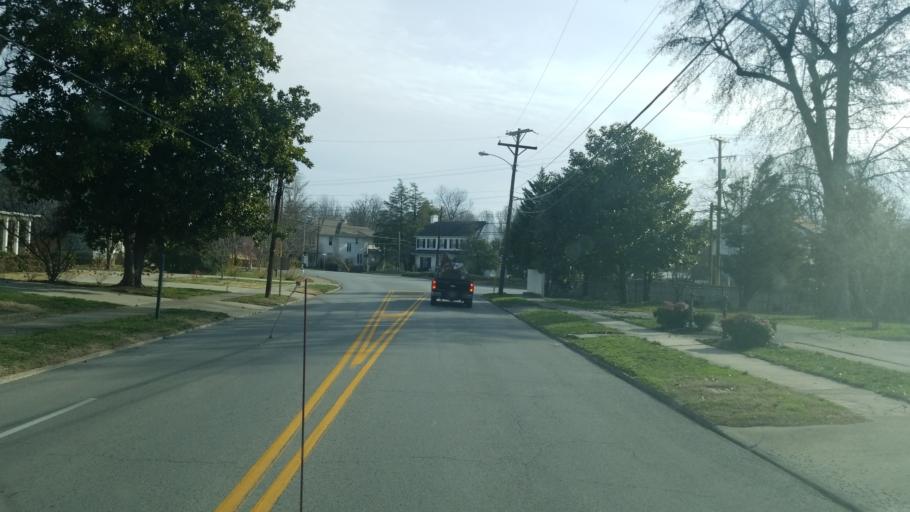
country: US
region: Kentucky
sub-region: Boyle County
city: Danville
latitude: 37.6485
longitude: -84.7651
